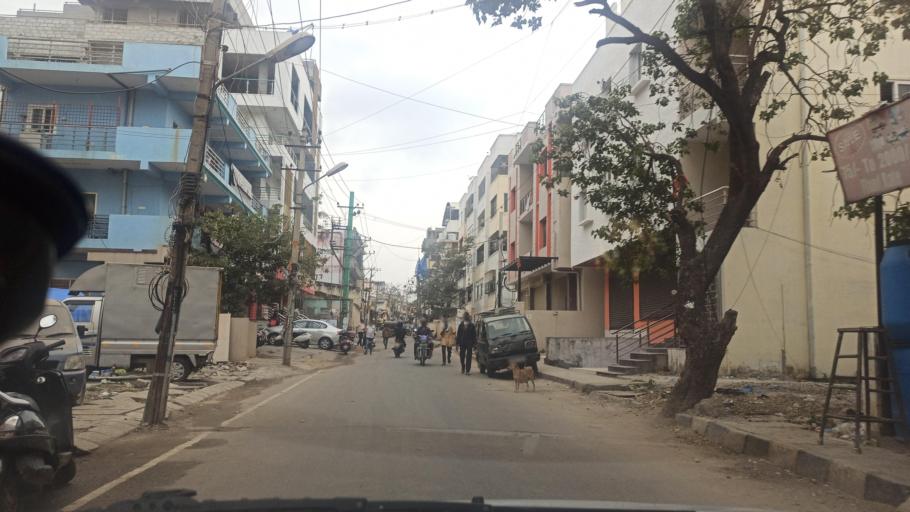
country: IN
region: Karnataka
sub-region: Bangalore Urban
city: Yelahanka
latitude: 13.0393
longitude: 77.5985
